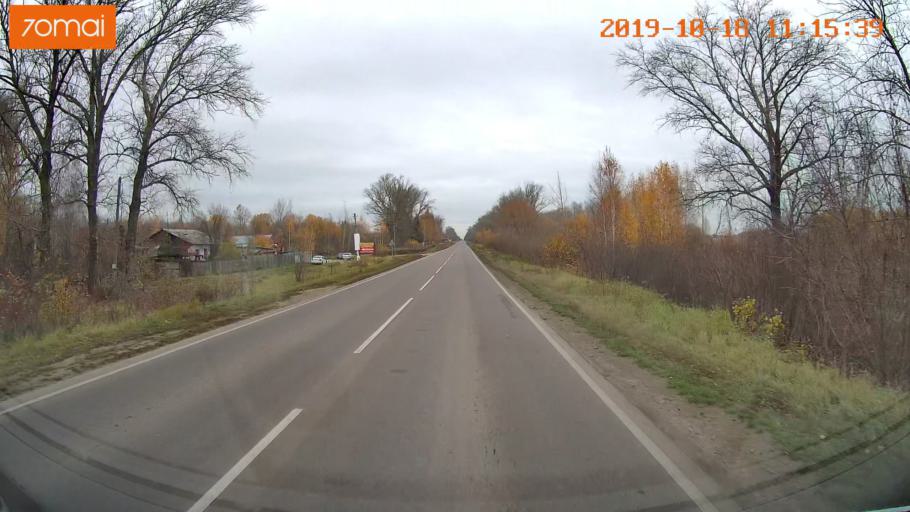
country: RU
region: Tula
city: Kimovsk
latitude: 53.9954
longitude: 38.5477
